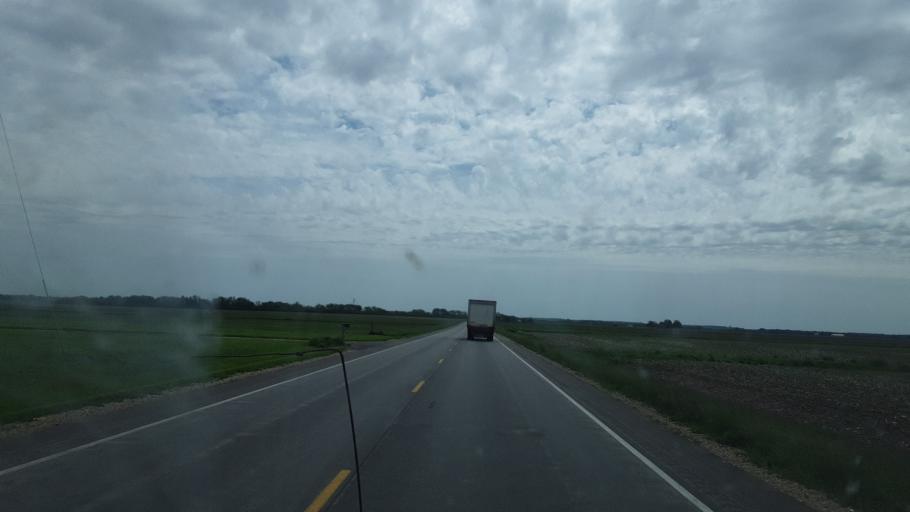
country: US
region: Illinois
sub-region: Tazewell County
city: Richmond
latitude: 40.3095
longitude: -89.3841
